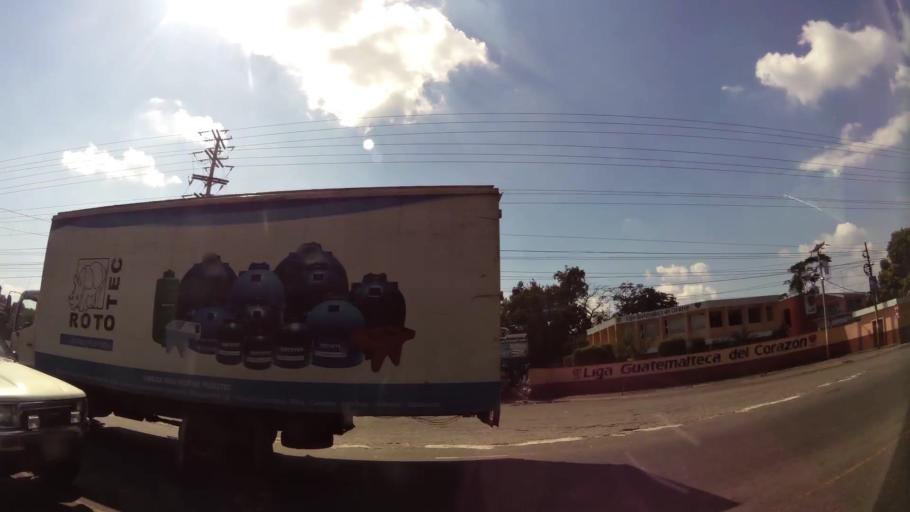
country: GT
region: Suchitepeque
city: Mazatenango
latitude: 14.5368
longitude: -91.4987
